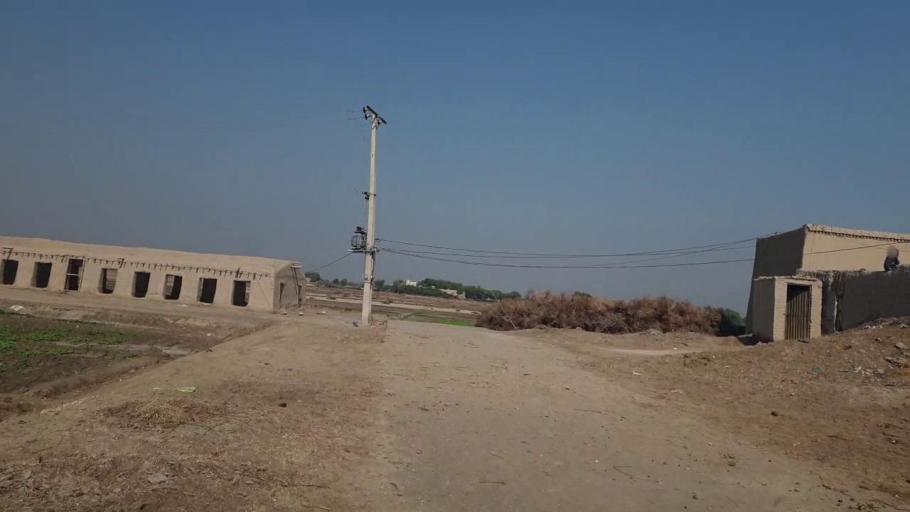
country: PK
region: Sindh
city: Sehwan
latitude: 26.4330
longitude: 67.7729
